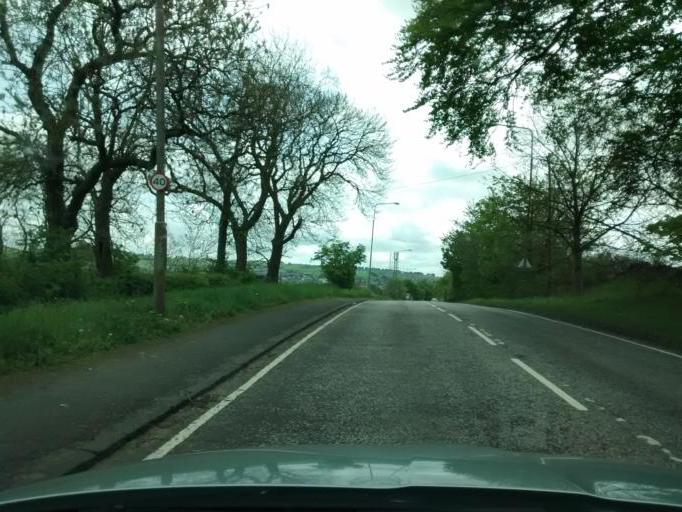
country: GB
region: Scotland
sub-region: West Lothian
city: Bathgate
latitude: 55.9003
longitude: -3.6718
